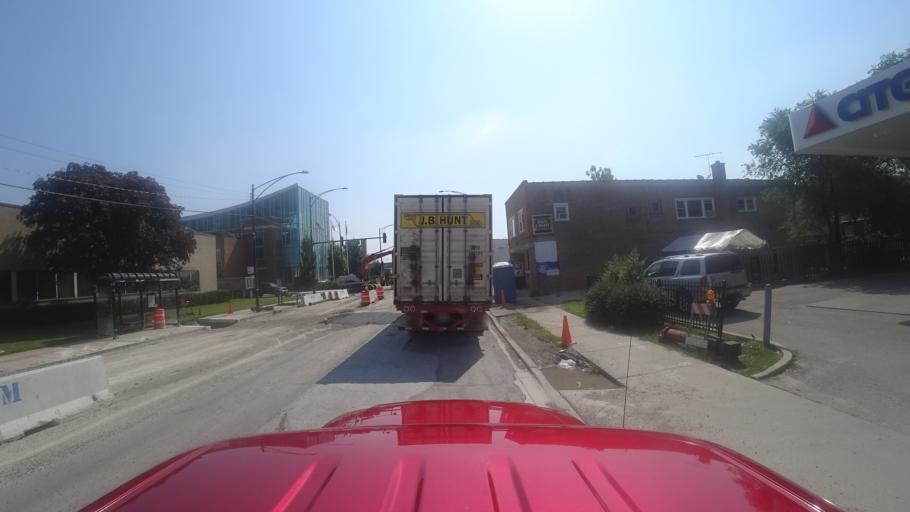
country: US
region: Illinois
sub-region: Cook County
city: Cicero
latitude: 41.8077
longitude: -87.7317
